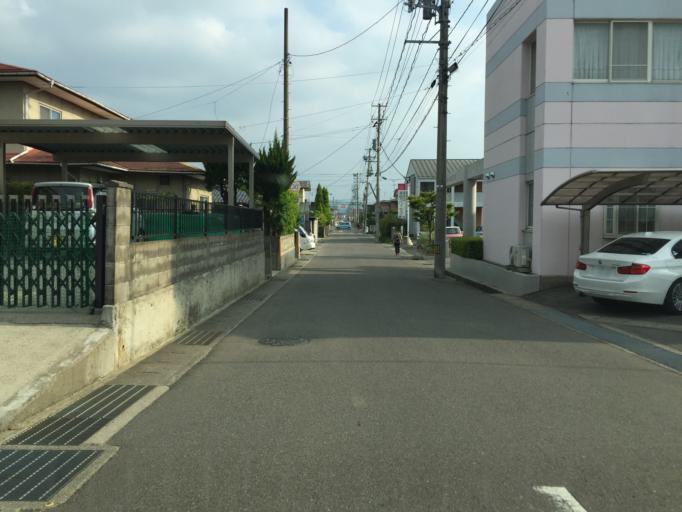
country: JP
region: Fukushima
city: Fukushima-shi
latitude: 37.7371
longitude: 140.4510
